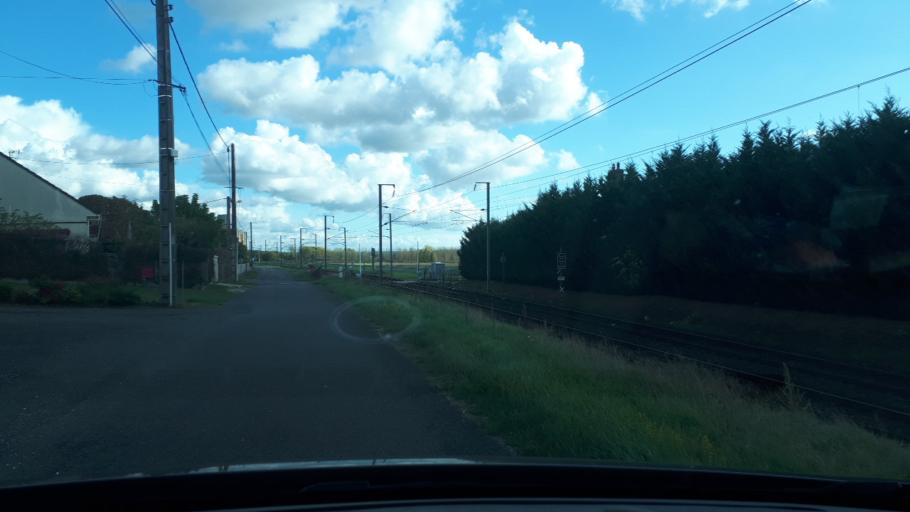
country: FR
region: Centre
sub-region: Departement du Loir-et-Cher
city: Mareuil-sur-Cher
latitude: 47.3013
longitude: 1.3535
